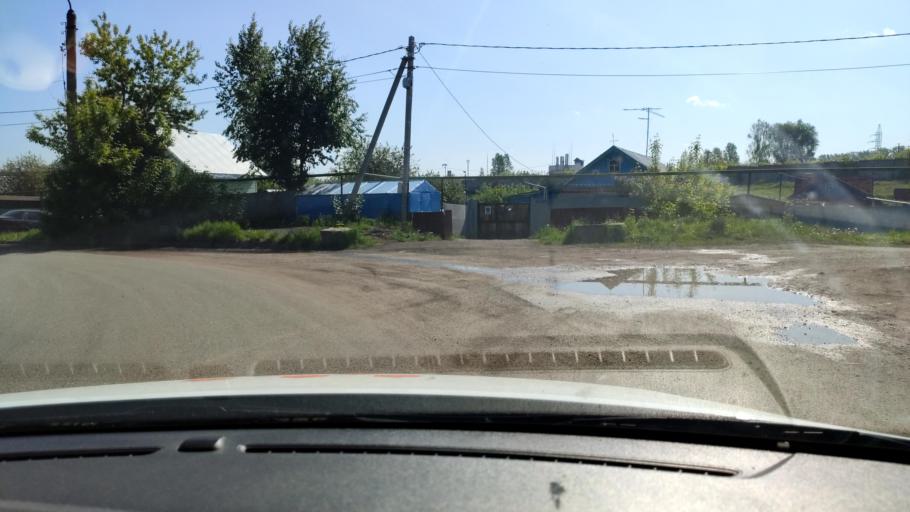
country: RU
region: Tatarstan
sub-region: Gorod Kazan'
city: Kazan
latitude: 55.7446
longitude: 49.1099
